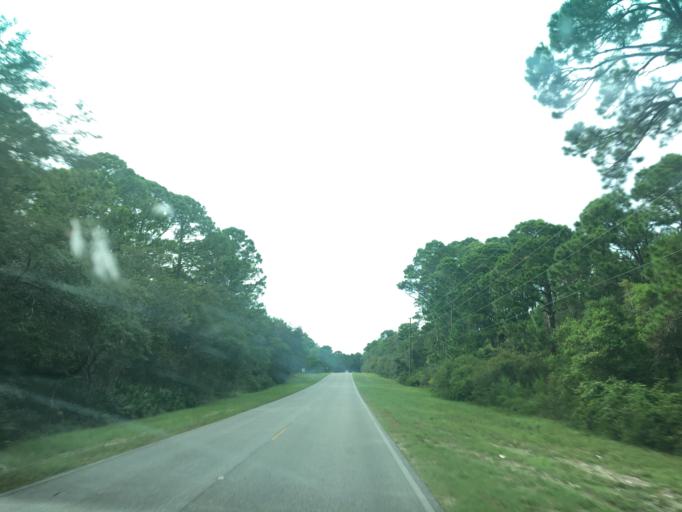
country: US
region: Florida
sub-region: Wakulla County
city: Crawfordville
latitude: 29.9244
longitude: -84.3749
